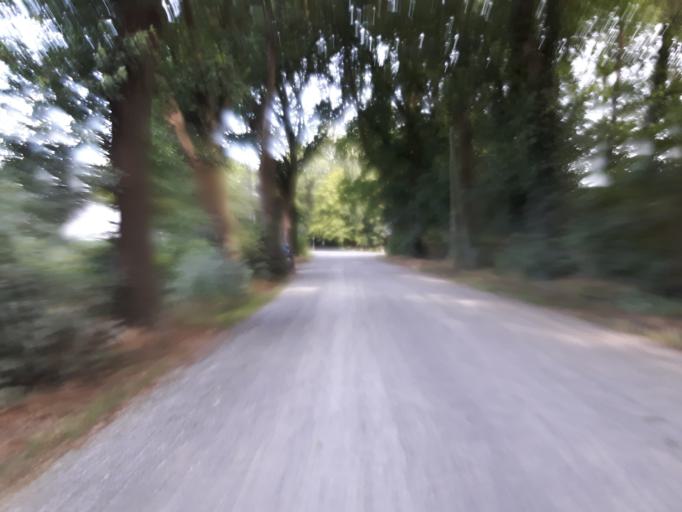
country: DE
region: Lower Saxony
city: Delmenhorst
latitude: 53.0863
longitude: 8.6185
